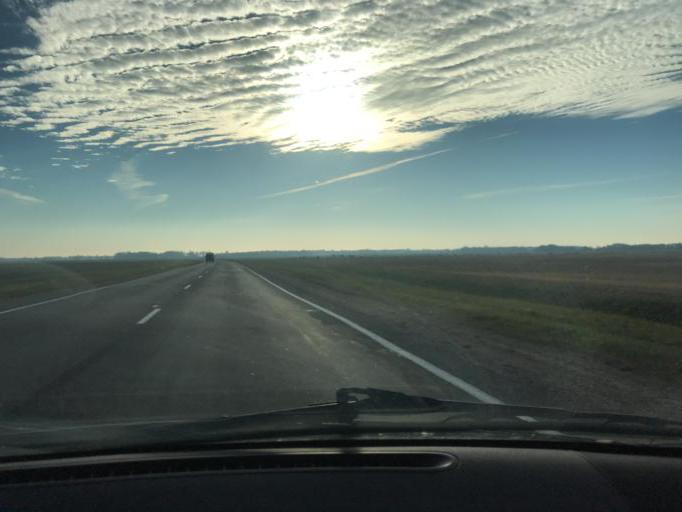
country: BY
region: Brest
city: Drahichyn
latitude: 52.2145
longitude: 25.1862
